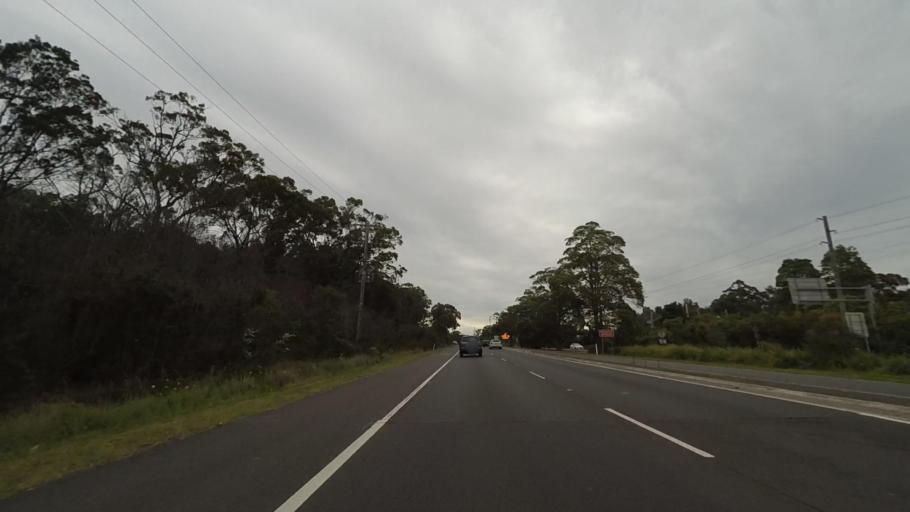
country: AU
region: New South Wales
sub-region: Sutherland Shire
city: Loftus
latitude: -34.0465
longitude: 151.0525
